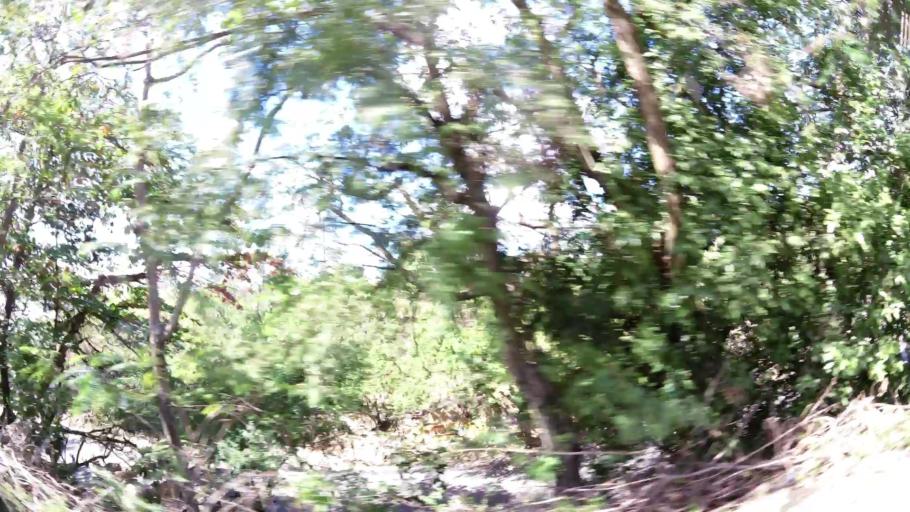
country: DO
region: San Cristobal
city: San Cristobal
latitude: 18.4285
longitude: -70.0837
